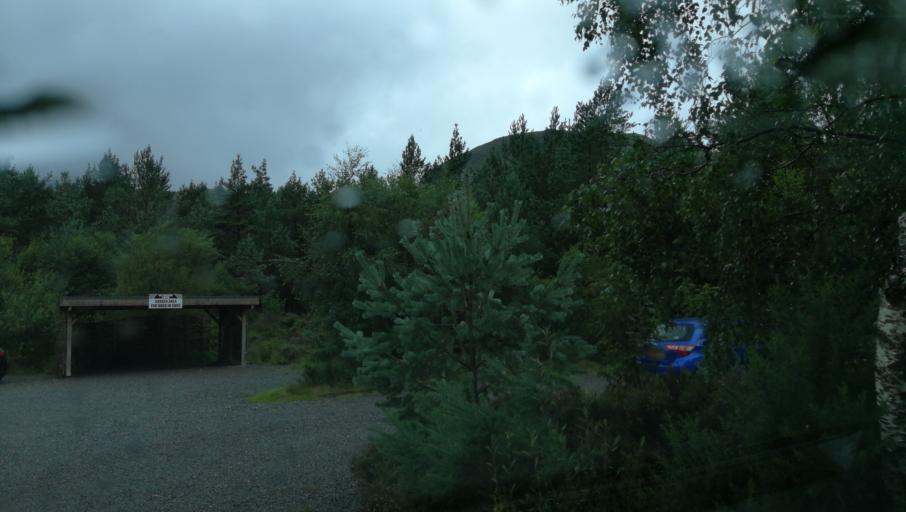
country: GB
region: Scotland
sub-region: Highland
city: Ullapool
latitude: 57.6131
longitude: -5.3169
